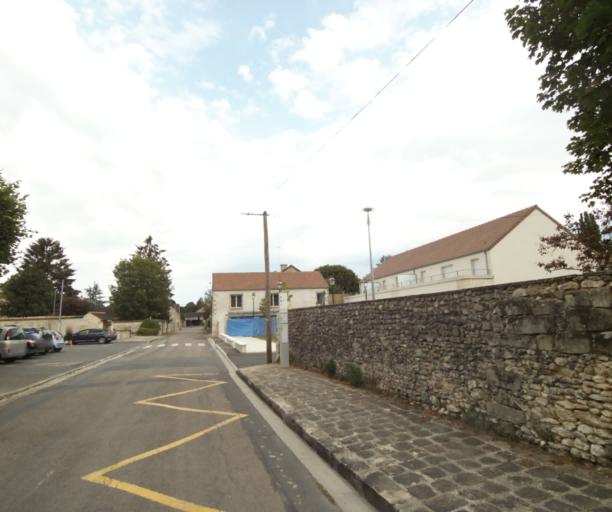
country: FR
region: Ile-de-France
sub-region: Departement de Seine-et-Marne
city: Cely
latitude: 48.4598
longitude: 2.5306
